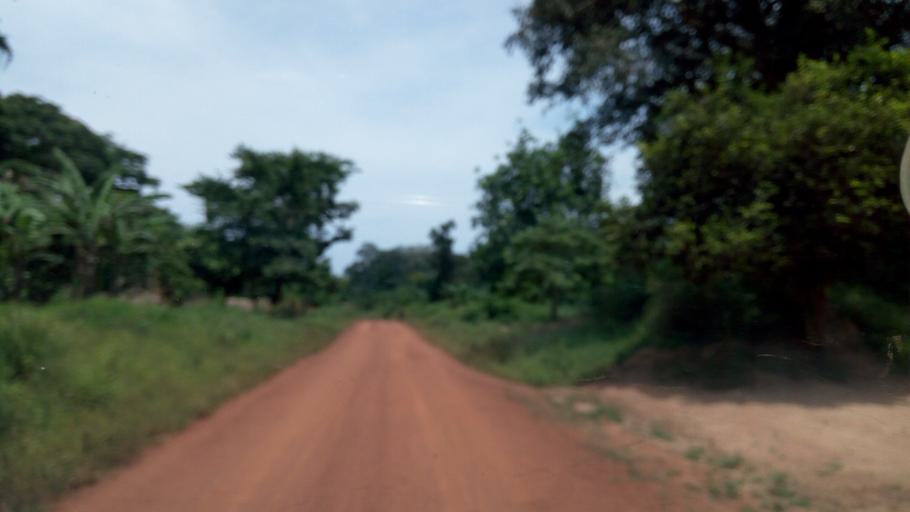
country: CD
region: Equateur
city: Gemena
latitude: 3.3168
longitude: 19.4205
